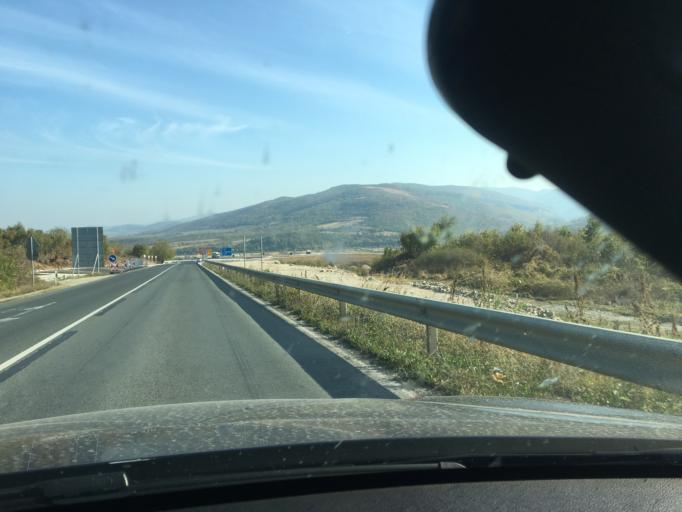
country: BG
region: Lovech
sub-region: Obshtina Yablanitsa
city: Yablanitsa
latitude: 43.0591
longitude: 24.2188
